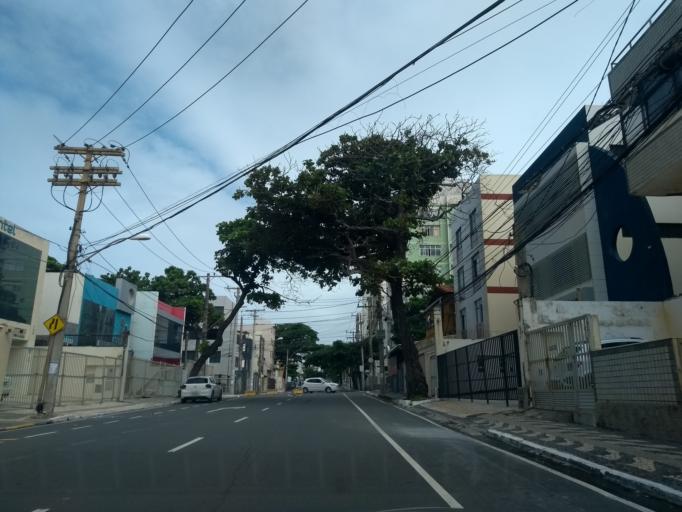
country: BR
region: Bahia
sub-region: Salvador
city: Salvador
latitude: -13.0031
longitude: -38.4533
